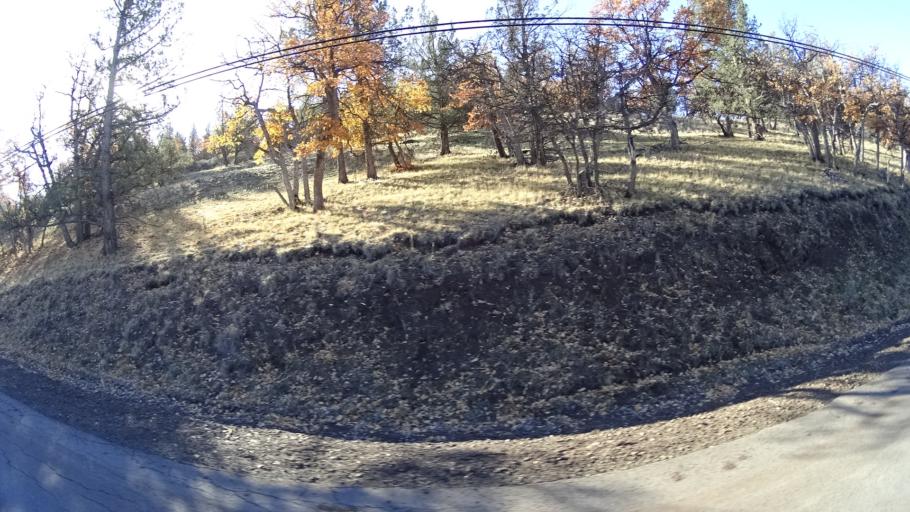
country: US
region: California
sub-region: Siskiyou County
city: Montague
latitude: 41.9150
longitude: -122.4363
